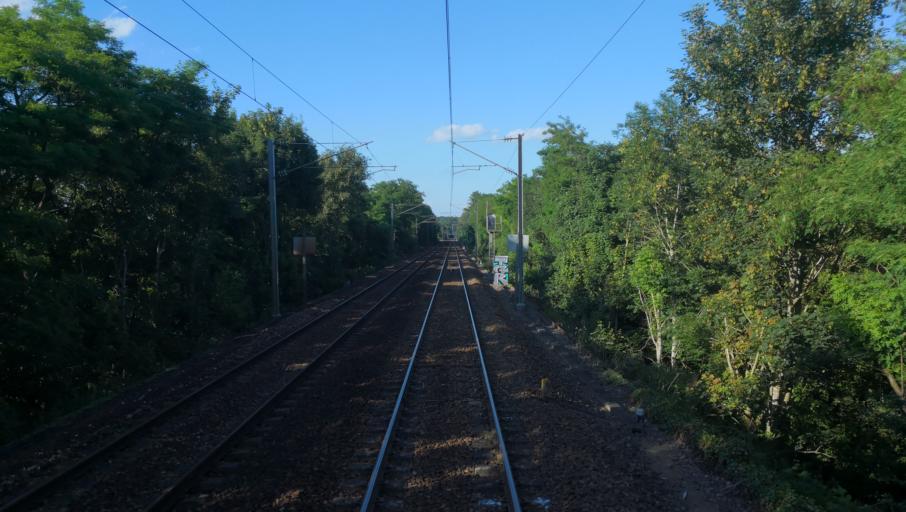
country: FR
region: Ile-de-France
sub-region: Departement des Yvelines
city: Rosny-sur-Seine
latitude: 48.9736
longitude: 1.6101
